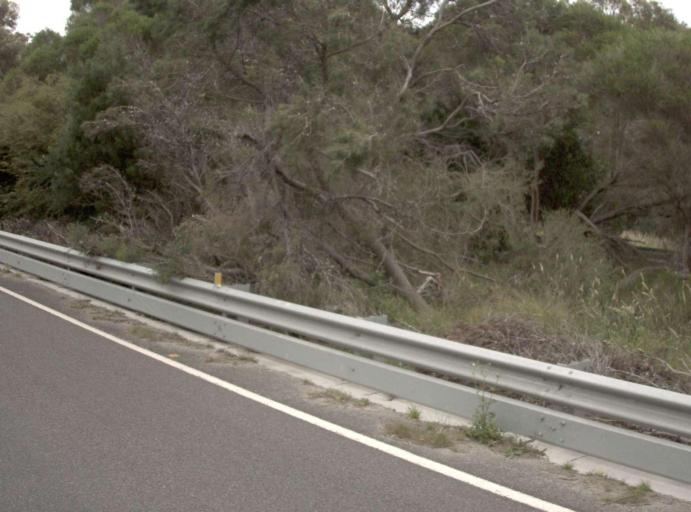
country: AU
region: Victoria
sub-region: Cardinia
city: Koo-Wee-Rup
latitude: -38.2896
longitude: 145.5461
